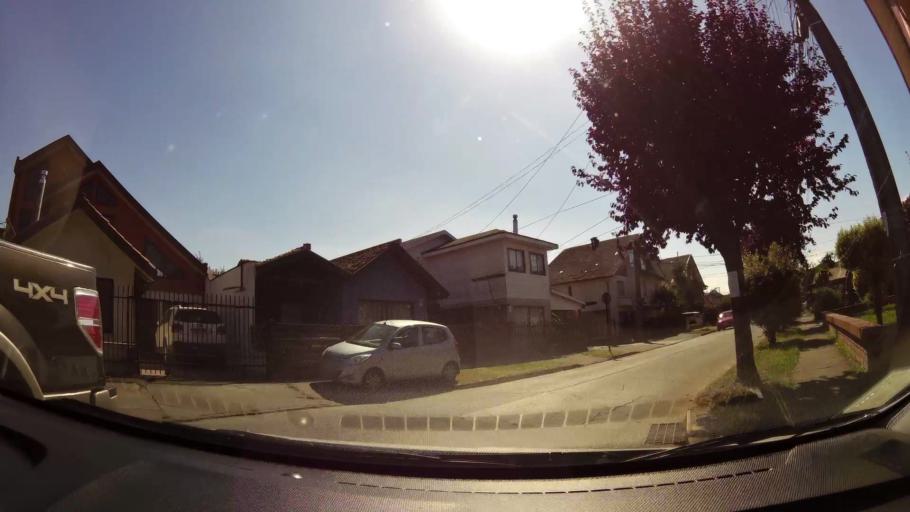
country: CL
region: Biobio
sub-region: Provincia de Concepcion
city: Concepcion
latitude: -36.7966
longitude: -73.0532
